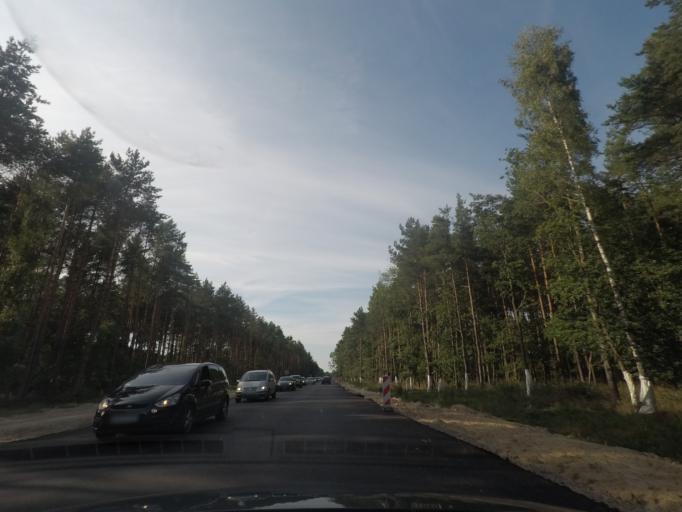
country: PL
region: Pomeranian Voivodeship
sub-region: Powiat leborski
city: Leba
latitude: 54.7156
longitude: 17.5766
